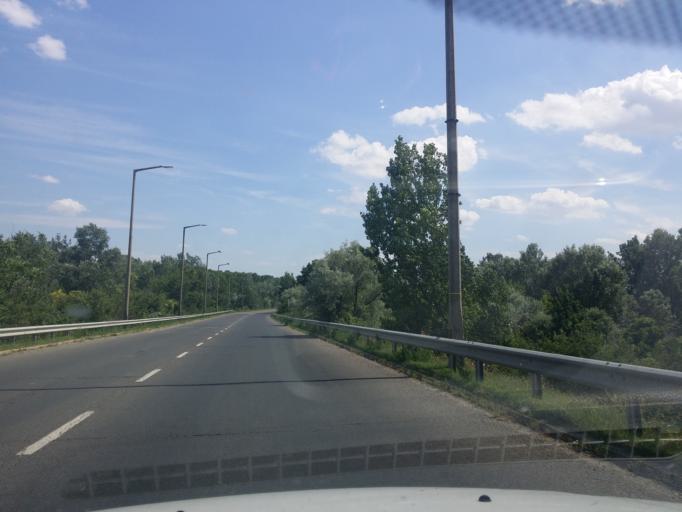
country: HU
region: Bacs-Kiskun
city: Kecskemet
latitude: 46.8967
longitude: 19.7047
